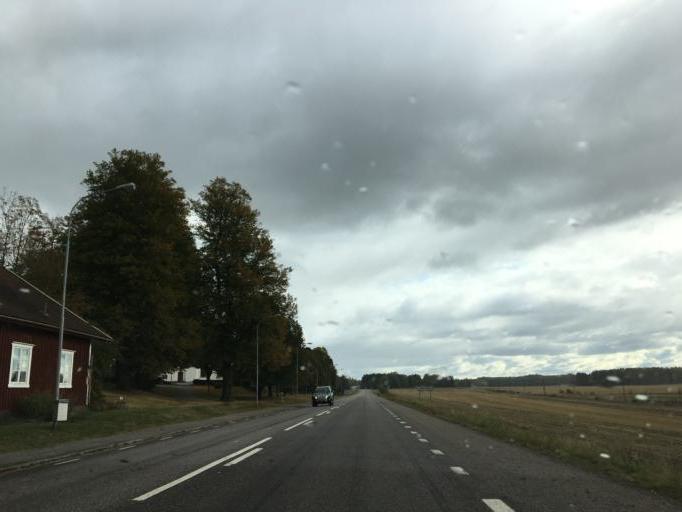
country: SE
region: Soedermanland
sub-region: Nykopings Kommun
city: Stigtomta
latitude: 58.7962
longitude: 16.7889
